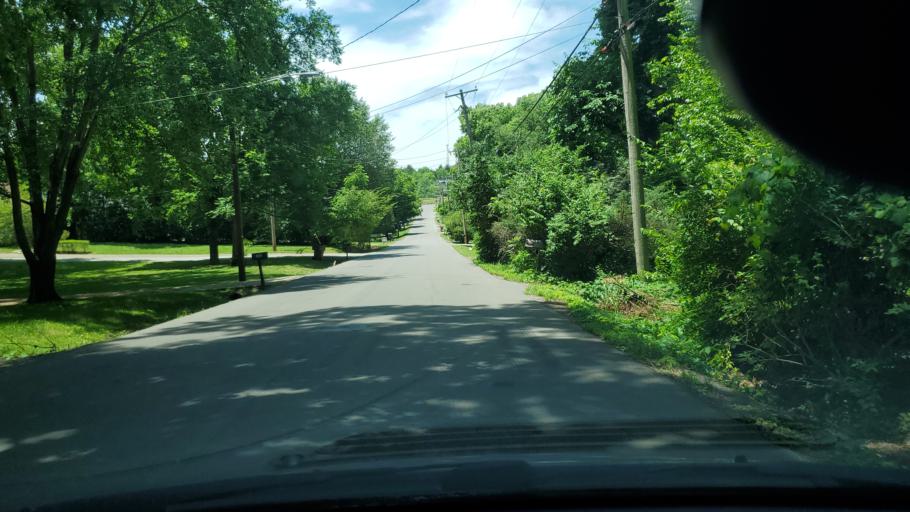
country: US
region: Tennessee
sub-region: Davidson County
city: Nashville
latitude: 36.2145
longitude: -86.7602
